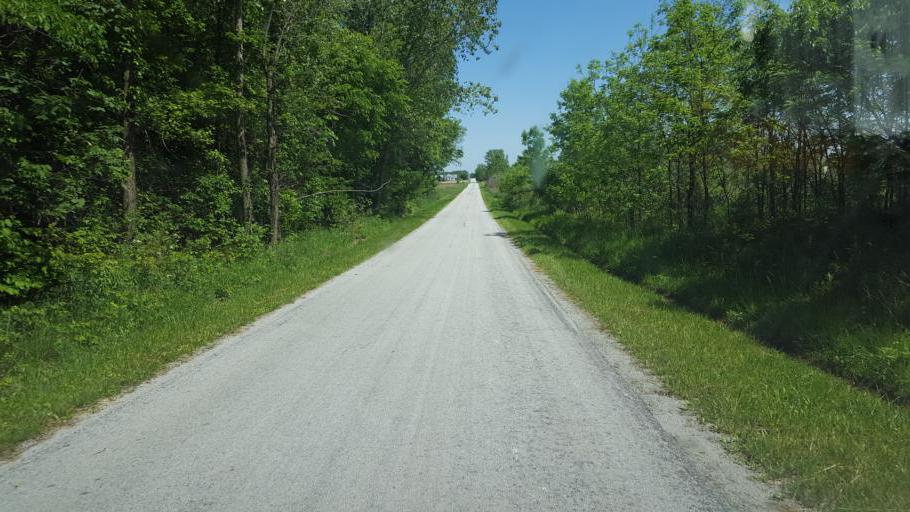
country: US
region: Ohio
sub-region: Hardin County
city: Kenton
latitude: 40.6377
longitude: -83.4388
